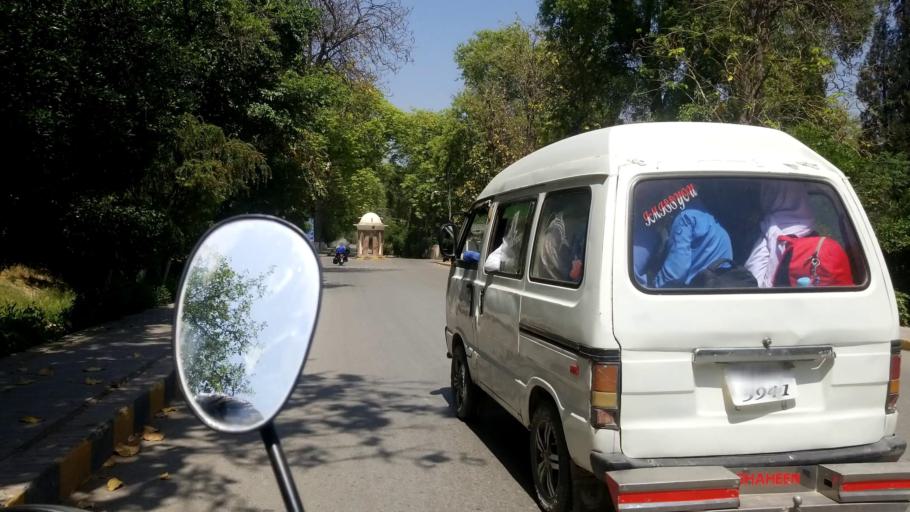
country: PK
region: Khyber Pakhtunkhwa
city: Peshawar
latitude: 34.0066
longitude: 71.4865
